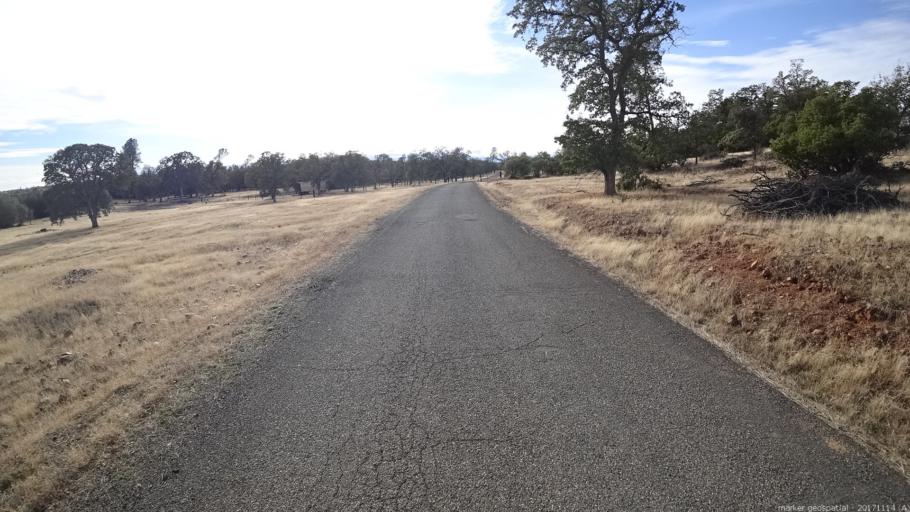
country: US
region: California
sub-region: Shasta County
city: Shasta
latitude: 40.3839
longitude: -122.5573
